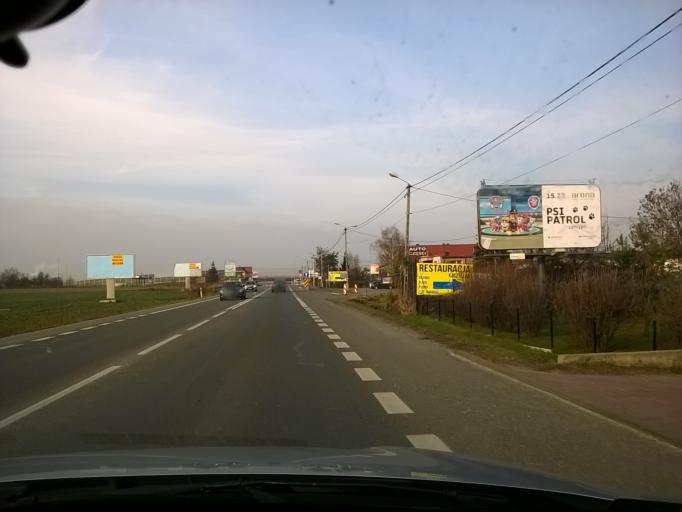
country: PL
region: Silesian Voivodeship
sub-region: Powiat gliwicki
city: Przyszowice
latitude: 50.2576
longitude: 18.7295
